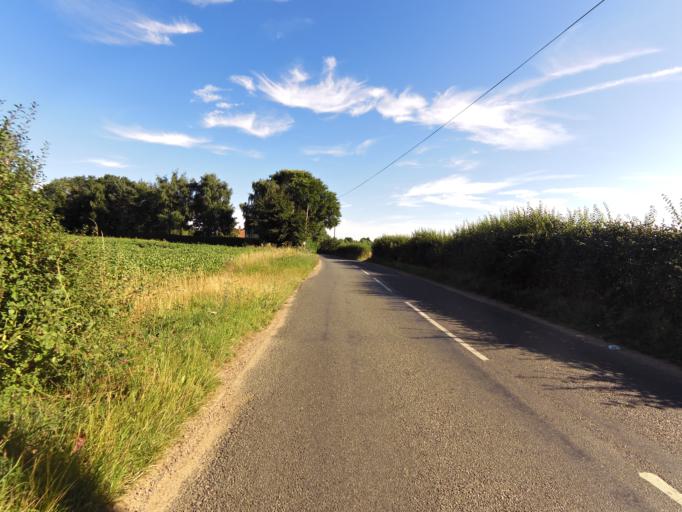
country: GB
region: England
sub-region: Suffolk
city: Kesgrave
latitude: 52.0345
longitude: 1.2613
